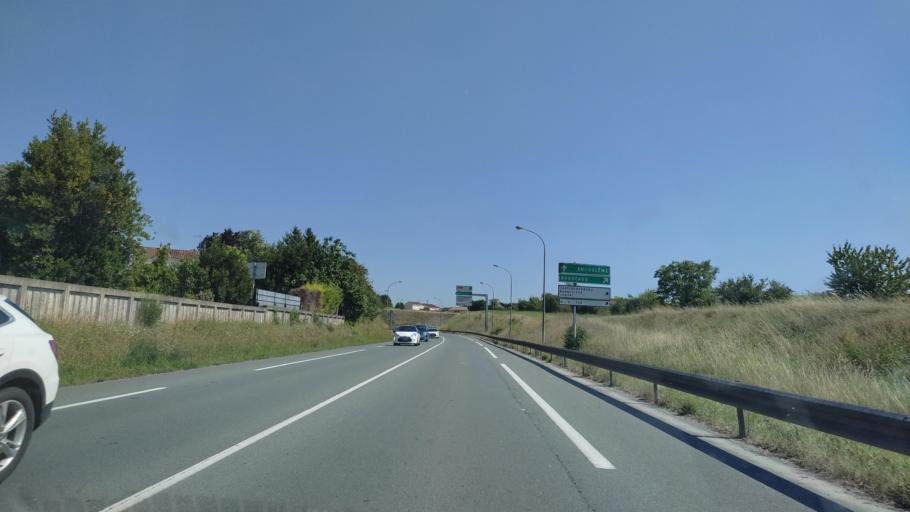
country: FR
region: Poitou-Charentes
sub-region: Departement de la Charente
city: Chateaubernard
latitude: 45.6780
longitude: -0.3317
